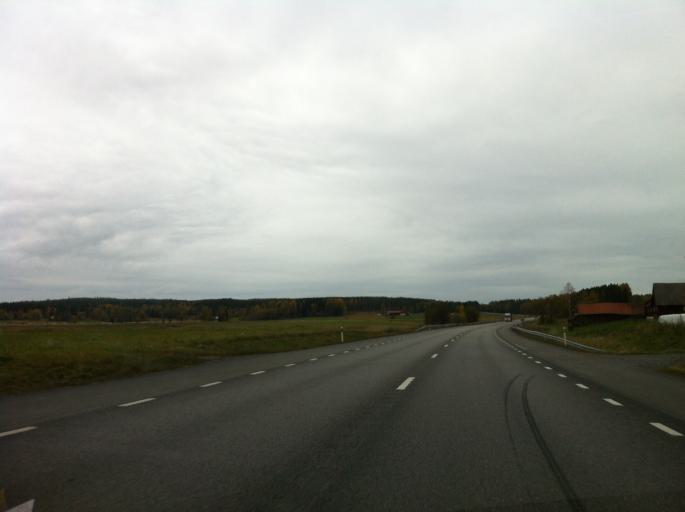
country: SE
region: OErebro
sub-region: Lindesbergs Kommun
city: Stora
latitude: 59.7554
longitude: 15.1448
